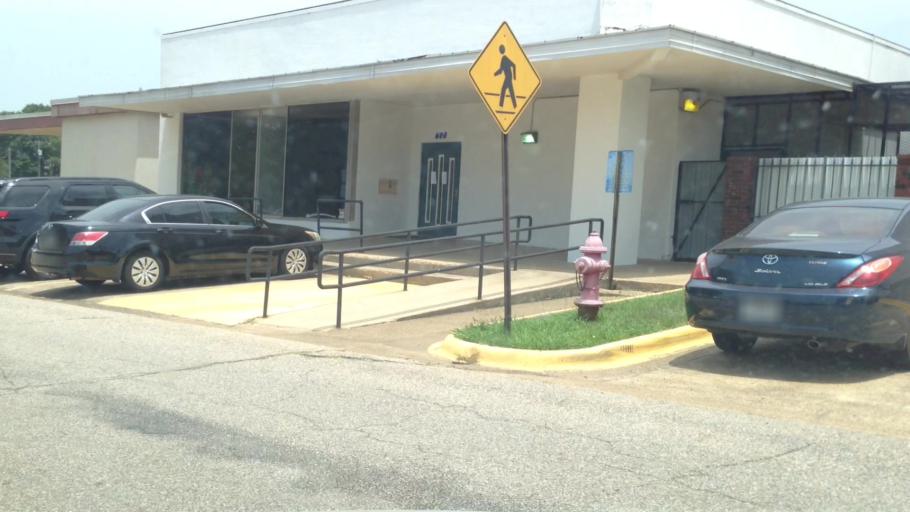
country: US
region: Texas
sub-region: Bowie County
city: Texarkana
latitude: 33.4265
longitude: -94.0421
